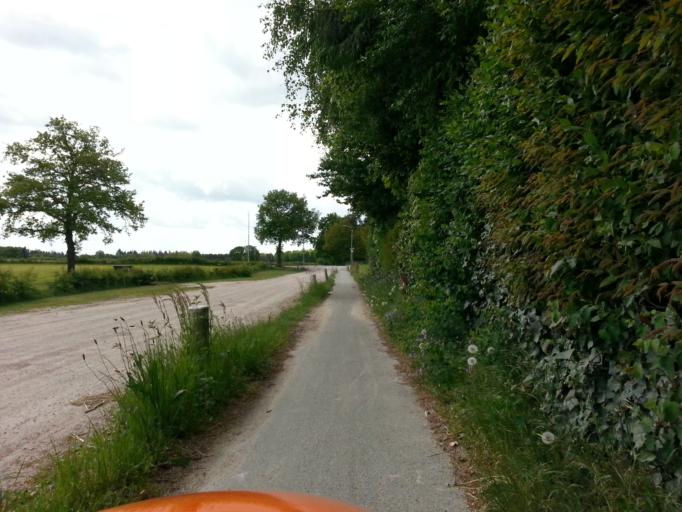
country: NL
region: Gelderland
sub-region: Gemeente Ede
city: Ede
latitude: 52.0616
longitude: 5.6486
